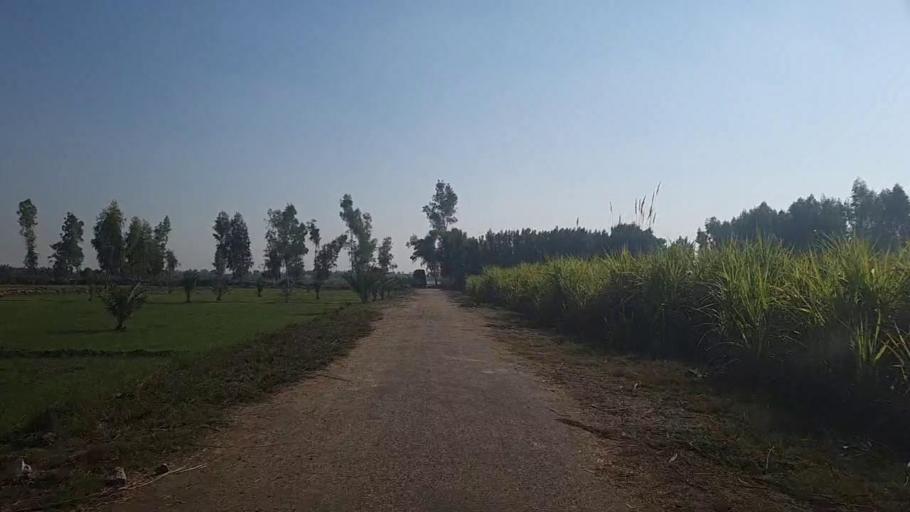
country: PK
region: Sindh
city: Kot Diji
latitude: 27.4326
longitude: 68.7315
